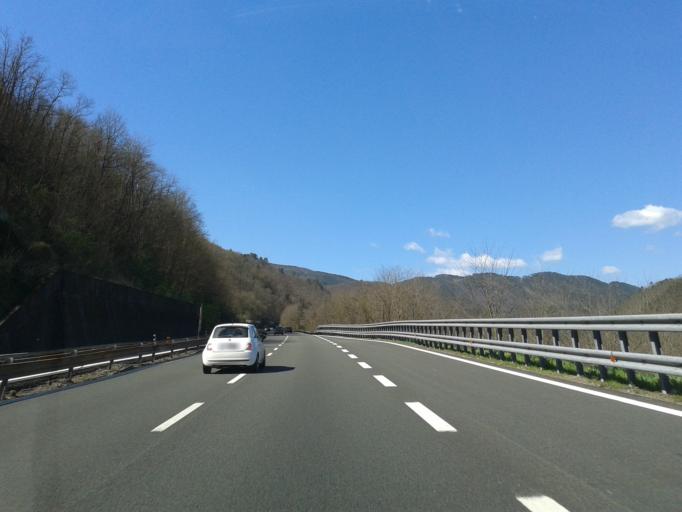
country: IT
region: Liguria
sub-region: Provincia di La Spezia
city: Carrodano
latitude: 44.2321
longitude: 9.6340
